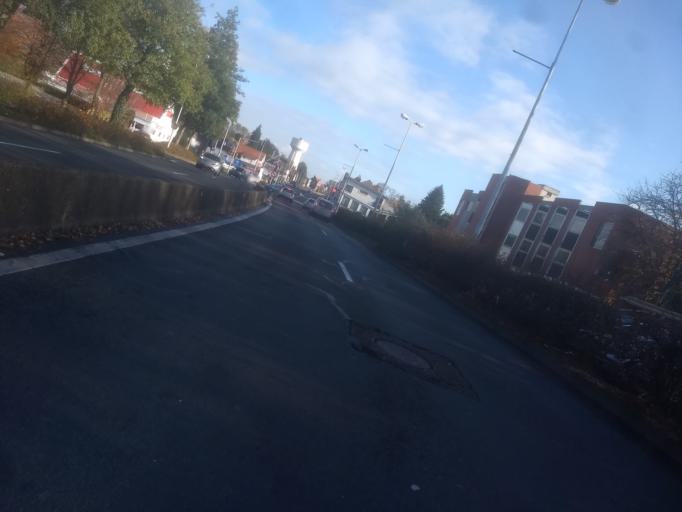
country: FR
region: Nord-Pas-de-Calais
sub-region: Departement du Pas-de-Calais
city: Sainte-Catherine
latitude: 50.2972
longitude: 2.7546
